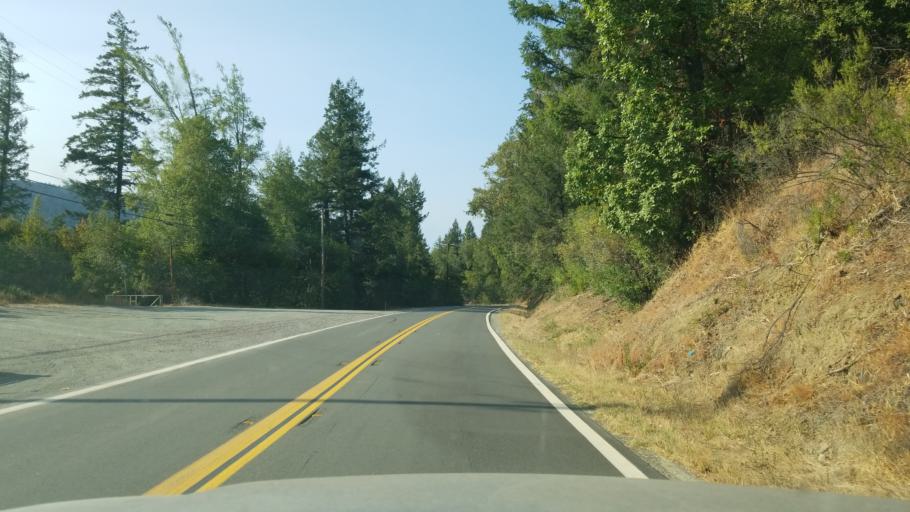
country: US
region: California
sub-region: Humboldt County
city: Redway
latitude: 40.2251
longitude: -123.8216
